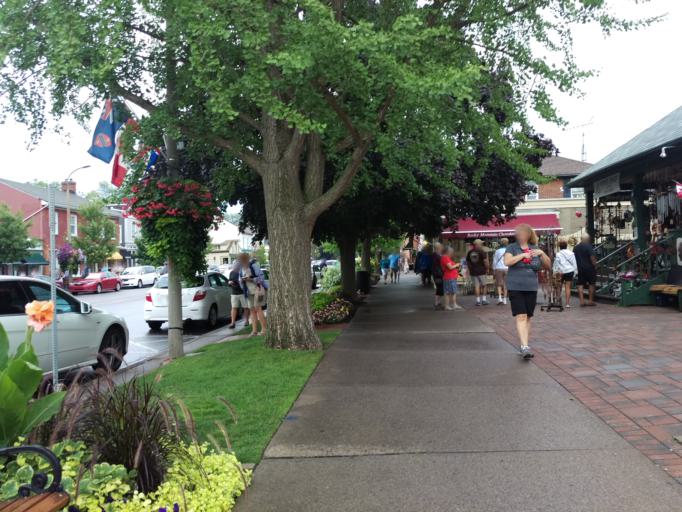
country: US
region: New York
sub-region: Niagara County
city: Youngstown
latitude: 43.2559
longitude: -79.0735
